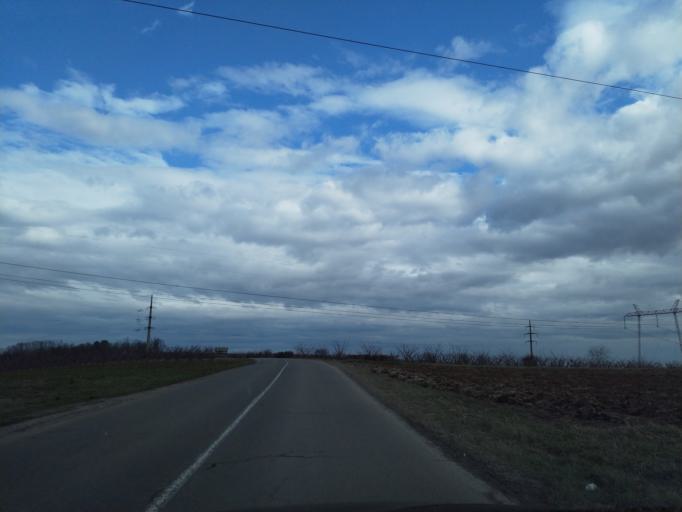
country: RS
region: Central Serbia
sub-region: Belgrade
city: Grocka
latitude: 44.6307
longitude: 20.7473
